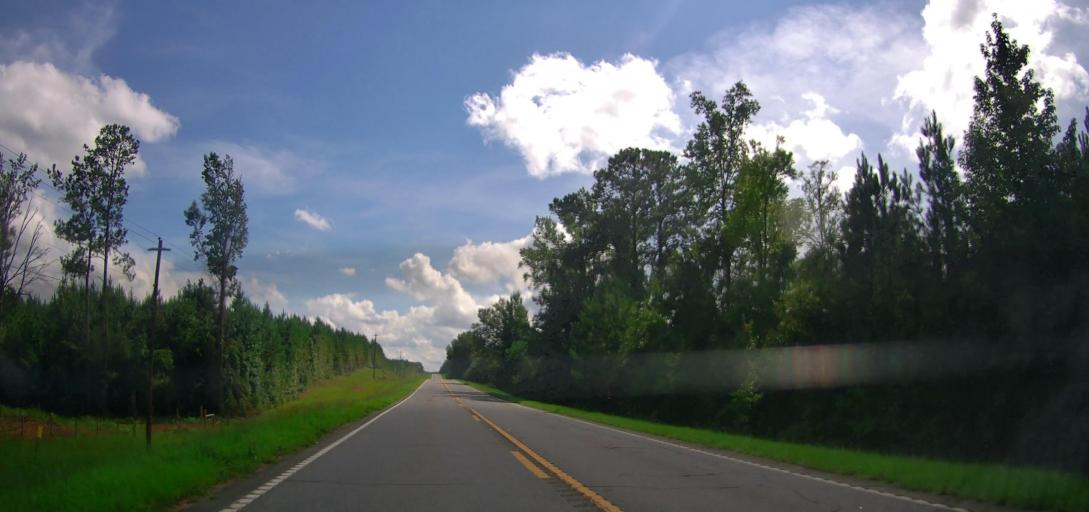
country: US
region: Georgia
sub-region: Talbot County
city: Talbotton
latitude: 32.7295
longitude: -84.5550
